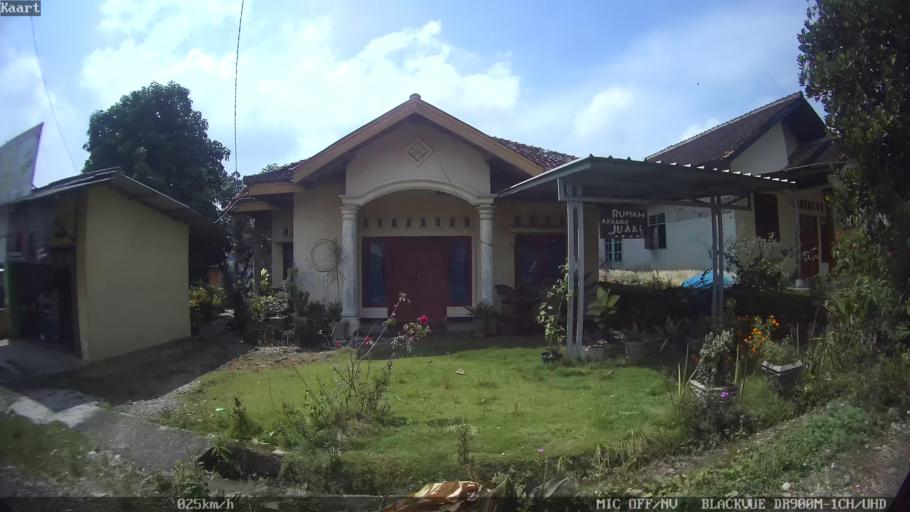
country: ID
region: Lampung
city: Kedaton
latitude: -5.3365
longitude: 105.2983
